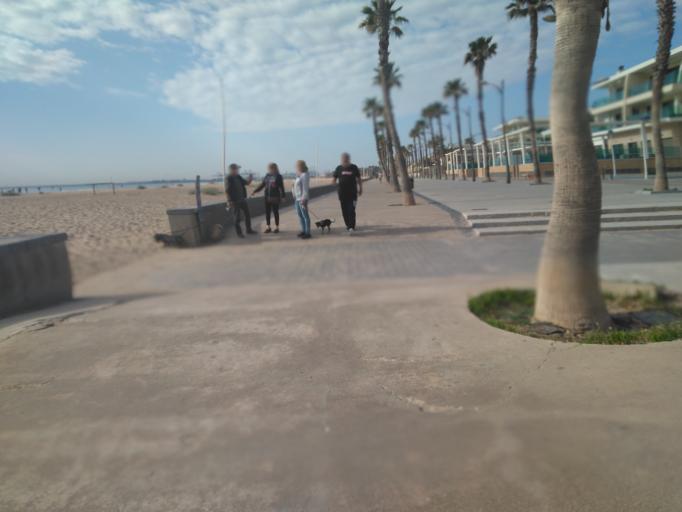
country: ES
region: Valencia
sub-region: Provincia de Valencia
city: Alboraya
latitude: 39.4916
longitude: -0.3245
